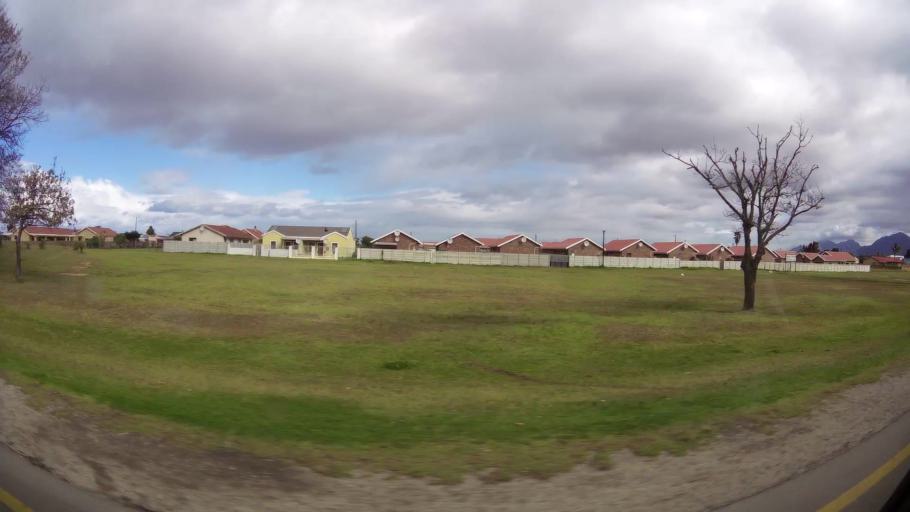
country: ZA
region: Western Cape
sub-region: Eden District Municipality
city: George
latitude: -33.9712
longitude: 22.4893
